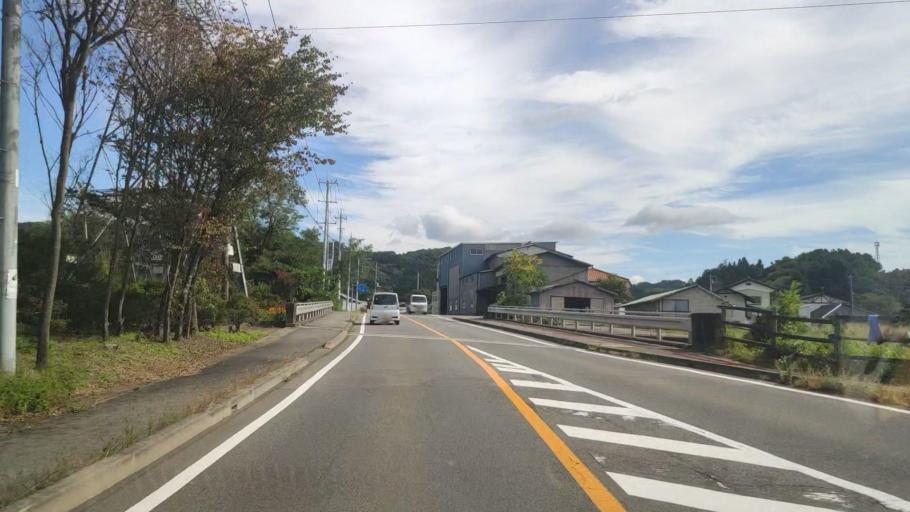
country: JP
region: Gunma
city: Numata
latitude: 36.6272
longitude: 138.9554
